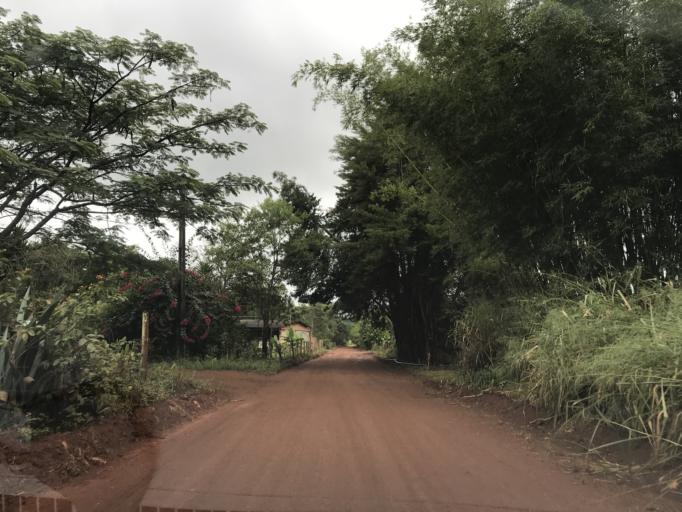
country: BR
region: Federal District
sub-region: Brasilia
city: Brasilia
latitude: -15.9186
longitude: -47.9292
